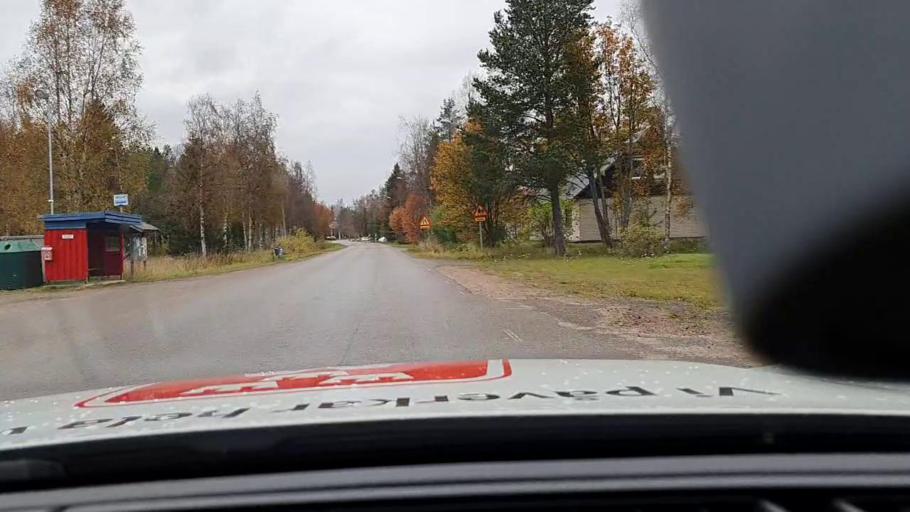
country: SE
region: Norrbotten
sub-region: Haparanda Kommun
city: Haparanda
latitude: 65.8035
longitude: 23.9185
